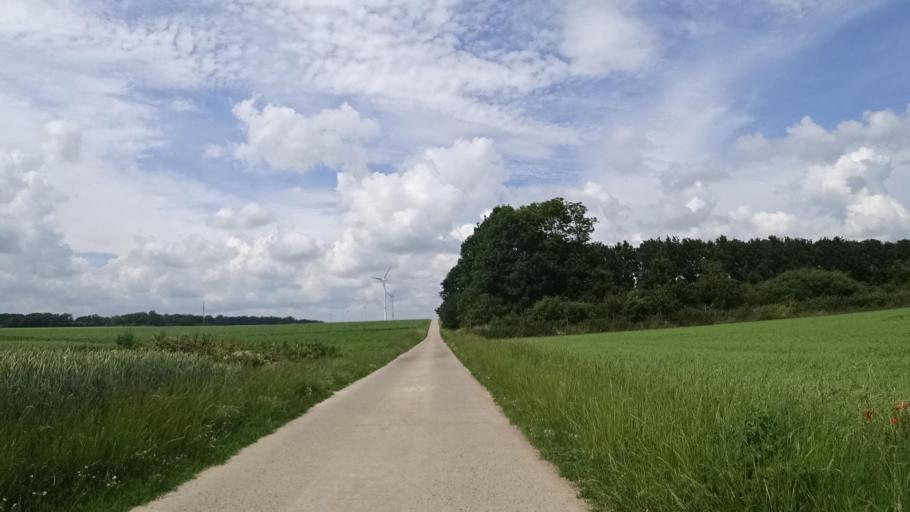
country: BE
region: Wallonia
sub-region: Province du Brabant Wallon
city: Perwez
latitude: 50.5816
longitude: 4.7999
